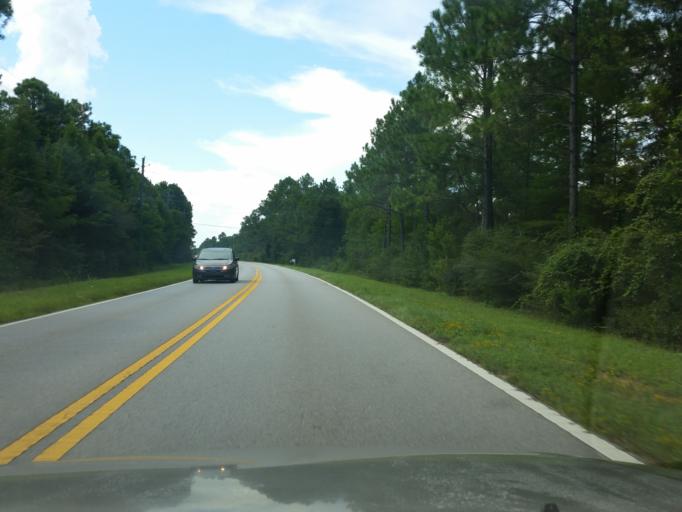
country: US
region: Florida
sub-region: Escambia County
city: Myrtle Grove
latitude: 30.3923
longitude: -87.4020
